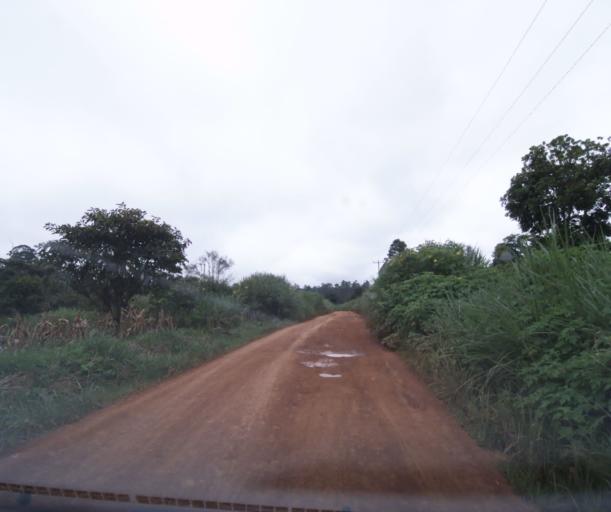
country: CM
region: West
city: Dschang
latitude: 5.5026
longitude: 10.0025
